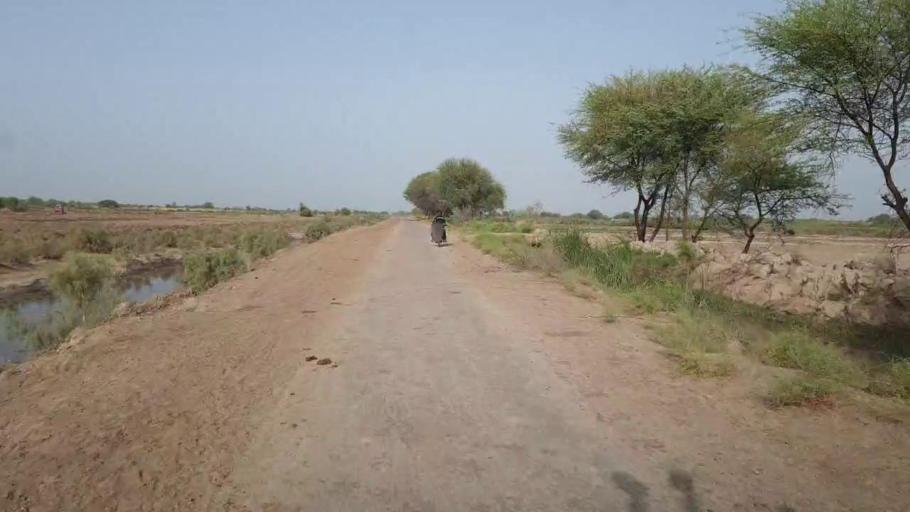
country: PK
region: Sindh
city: Daur
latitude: 26.3401
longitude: 68.2322
